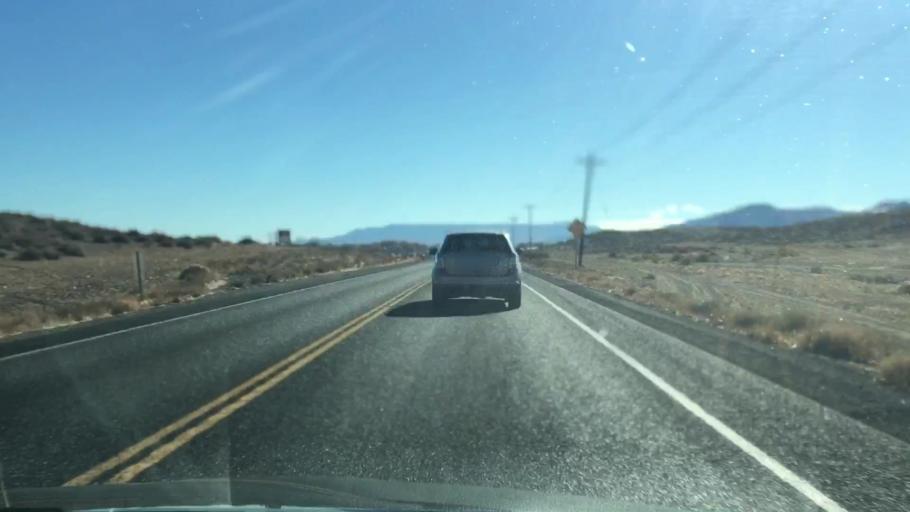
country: US
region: Nevada
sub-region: Lyon County
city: Yerington
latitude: 39.0090
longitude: -119.1828
